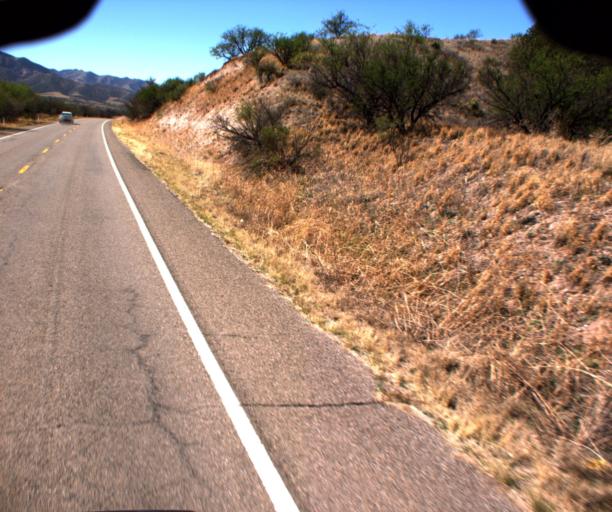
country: US
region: Arizona
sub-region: Santa Cruz County
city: Rio Rico
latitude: 31.5690
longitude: -110.7308
